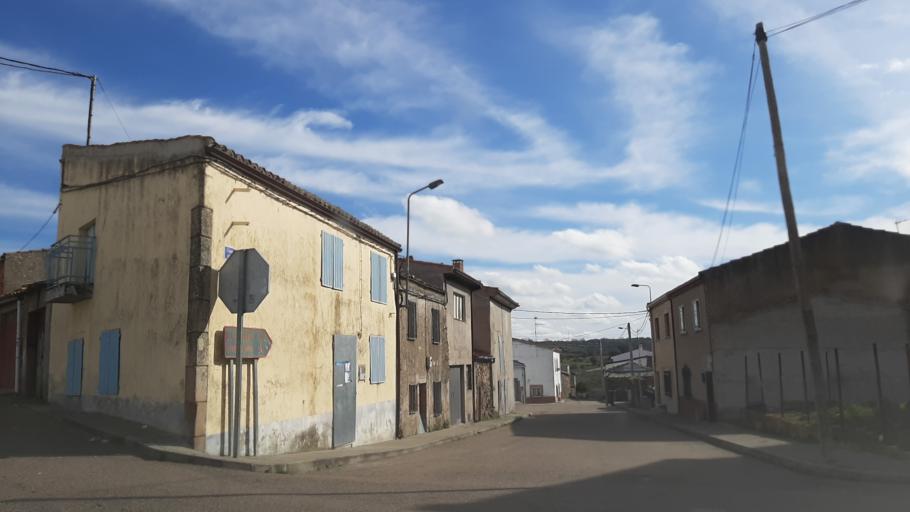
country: ES
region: Castille and Leon
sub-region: Provincia de Salamanca
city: Villarino de los Aires
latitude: 41.2366
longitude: -6.5228
